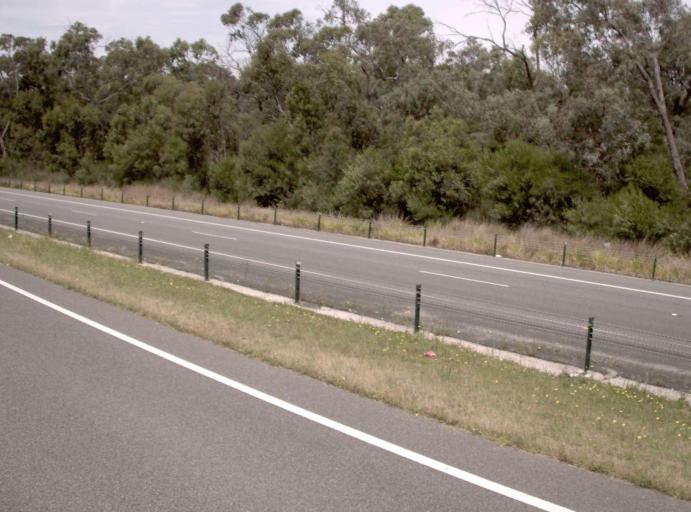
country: AU
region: Victoria
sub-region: Casey
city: Cranbourne South
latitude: -38.1652
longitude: 145.2225
